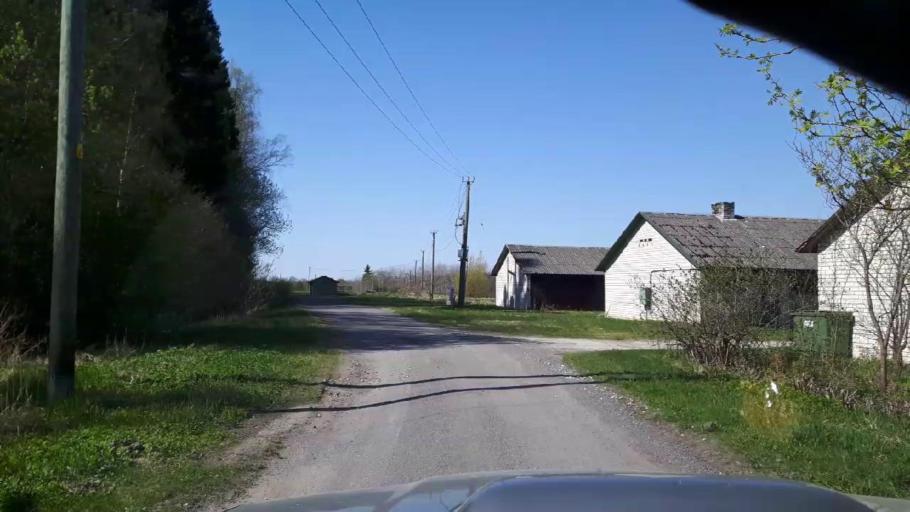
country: EE
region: Paernumaa
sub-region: Tootsi vald
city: Tootsi
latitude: 58.4741
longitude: 24.7913
